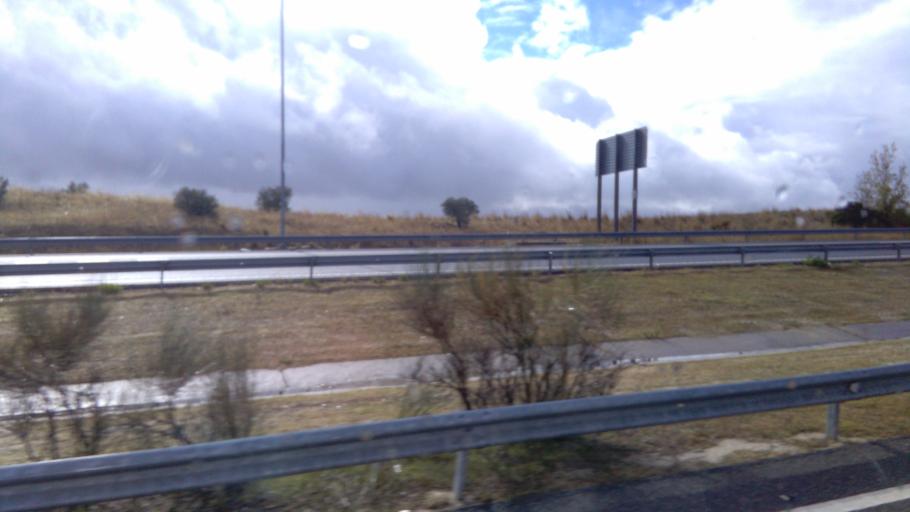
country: ES
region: Madrid
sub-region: Provincia de Madrid
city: El Alamo
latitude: 40.2597
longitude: -3.9821
